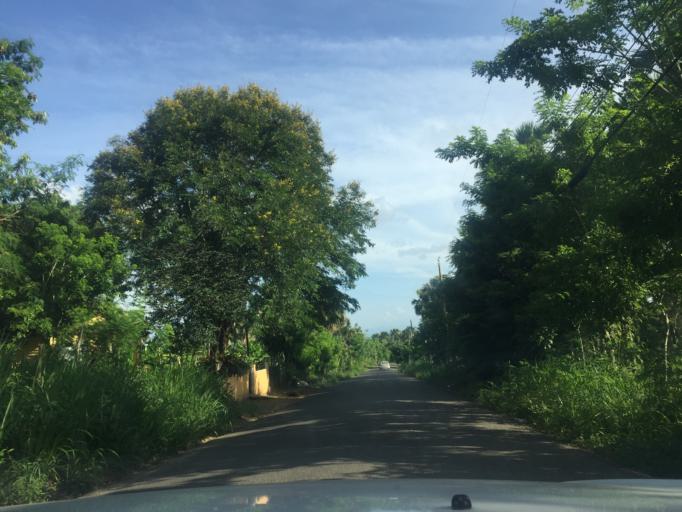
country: DO
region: Santiago
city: Tamboril
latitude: 19.4960
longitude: -70.6347
